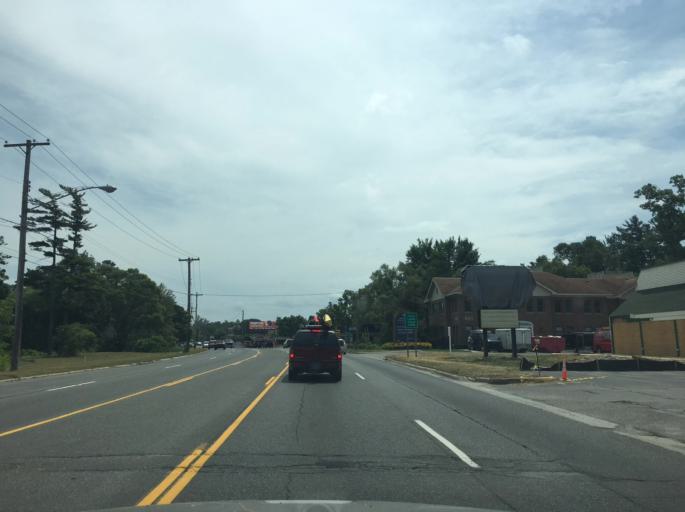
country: US
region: Michigan
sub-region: Grand Traverse County
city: Traverse City
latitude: 44.7499
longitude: -85.5613
